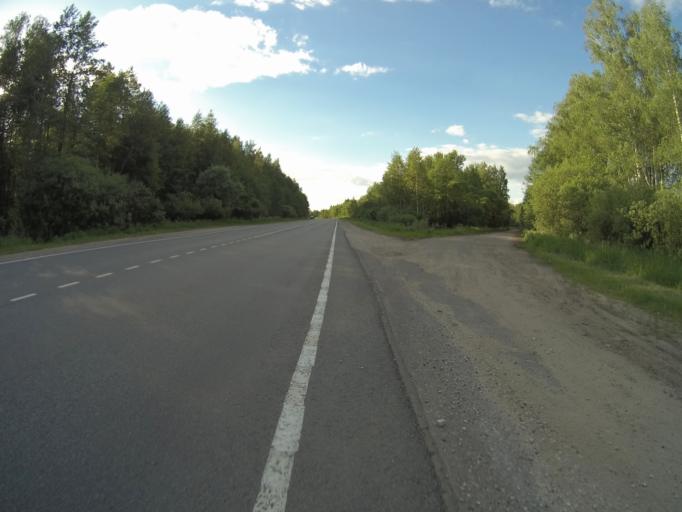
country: RU
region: Vladimir
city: Anopino
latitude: 55.8179
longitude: 40.6621
